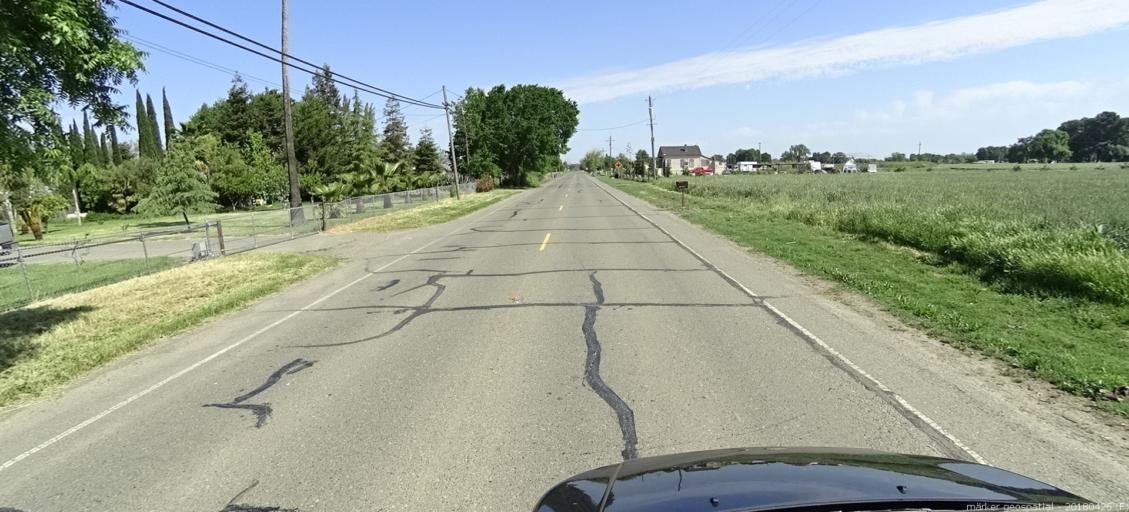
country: US
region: California
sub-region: Yolo County
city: West Sacramento
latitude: 38.5213
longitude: -121.5560
